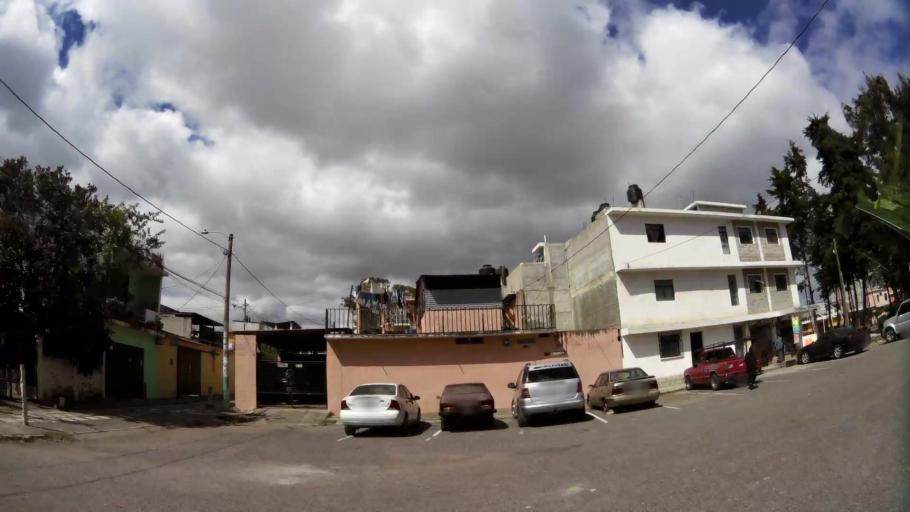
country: GT
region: Guatemala
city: Guatemala City
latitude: 14.6344
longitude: -90.5572
